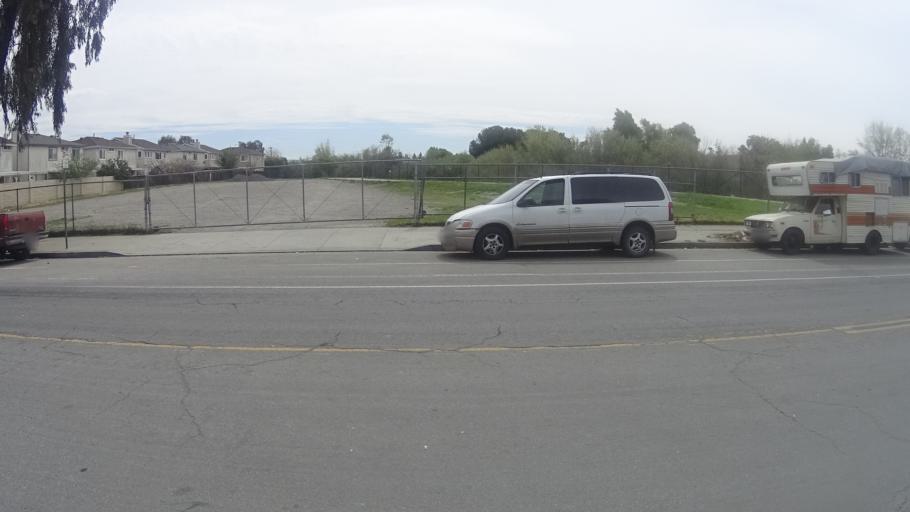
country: US
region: California
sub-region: Santa Clara County
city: Alum Rock
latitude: 37.3538
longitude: -121.8445
